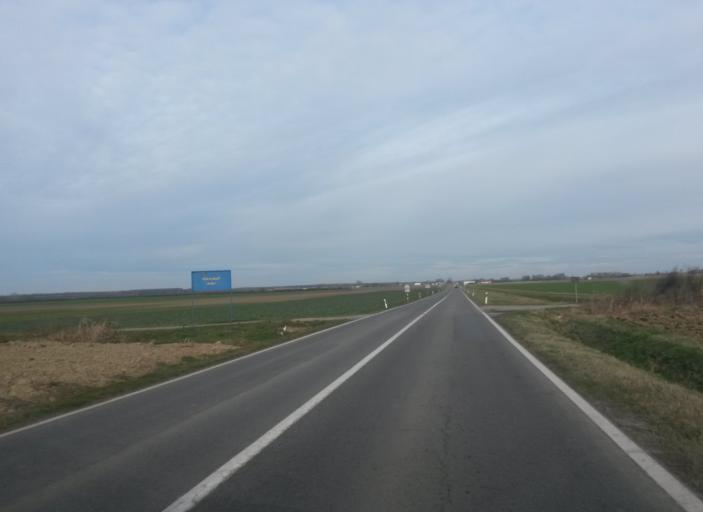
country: HR
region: Osjecko-Baranjska
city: Viskovci
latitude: 45.3828
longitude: 18.4460
